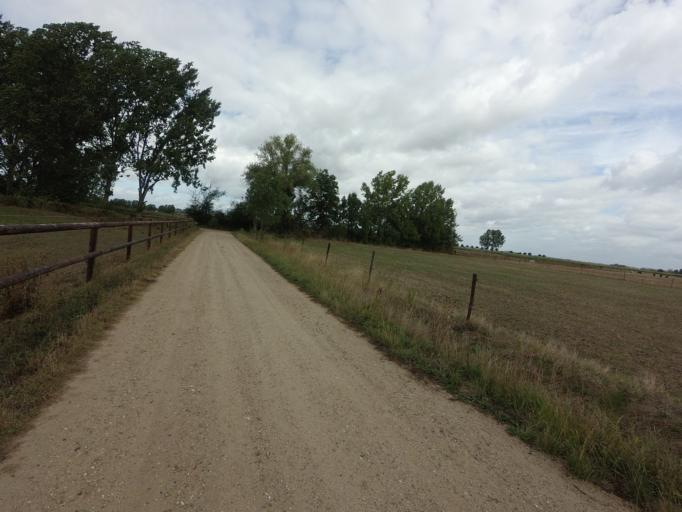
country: BE
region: Flanders
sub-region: Provincie Limburg
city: Maaseik
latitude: 51.1245
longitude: 5.8277
